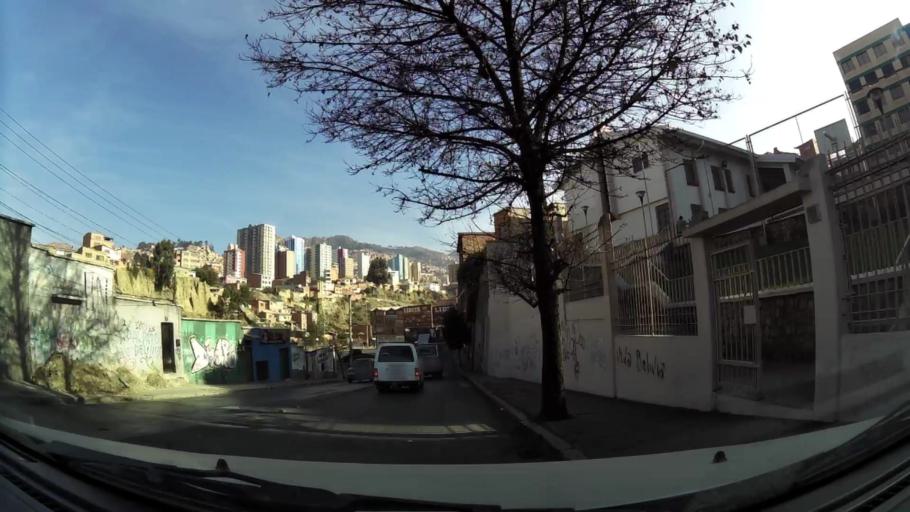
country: BO
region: La Paz
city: La Paz
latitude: -16.4953
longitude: -68.1180
